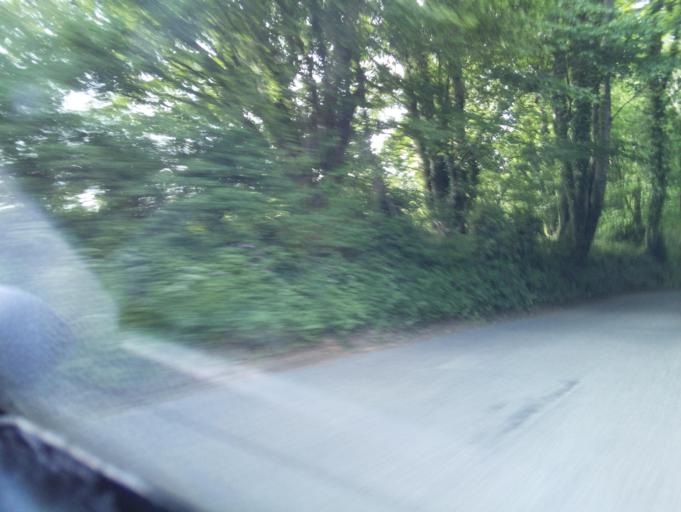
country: GB
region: England
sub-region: Gloucestershire
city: Westfield
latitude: 51.9127
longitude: -1.8530
